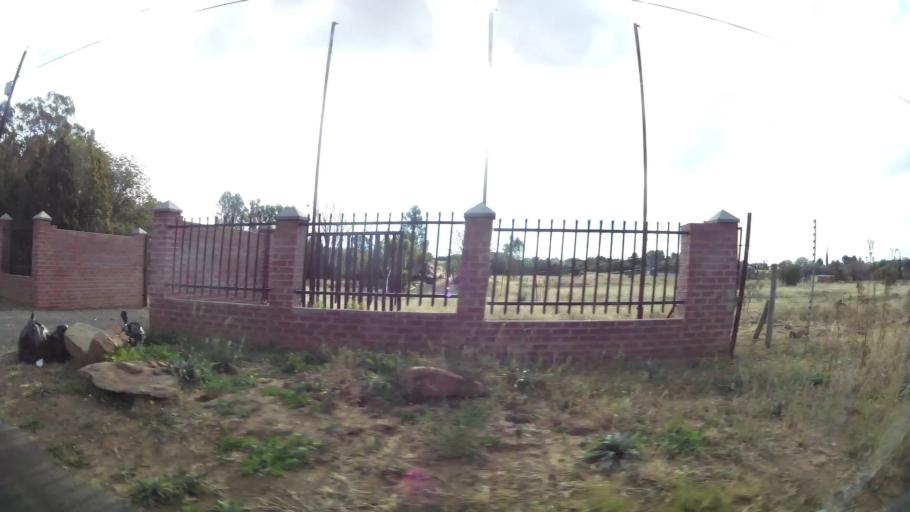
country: ZA
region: Orange Free State
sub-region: Mangaung Metropolitan Municipality
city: Bloemfontein
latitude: -29.0721
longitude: 26.1947
